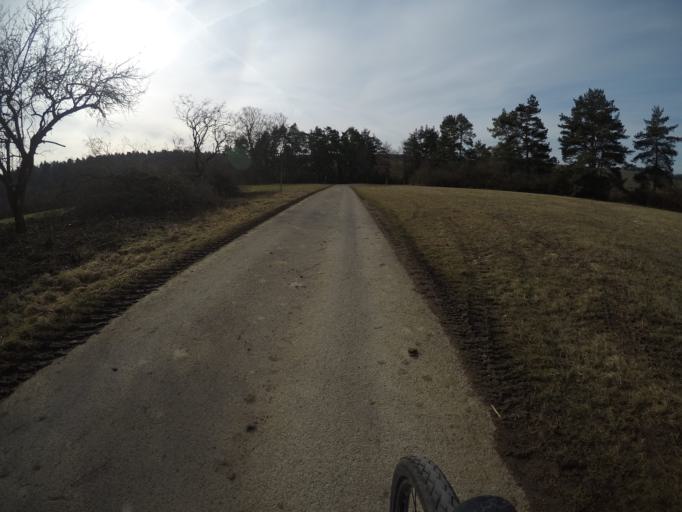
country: DE
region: Baden-Wuerttemberg
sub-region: Karlsruhe Region
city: Ostelsheim
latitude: 48.7092
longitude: 8.8683
